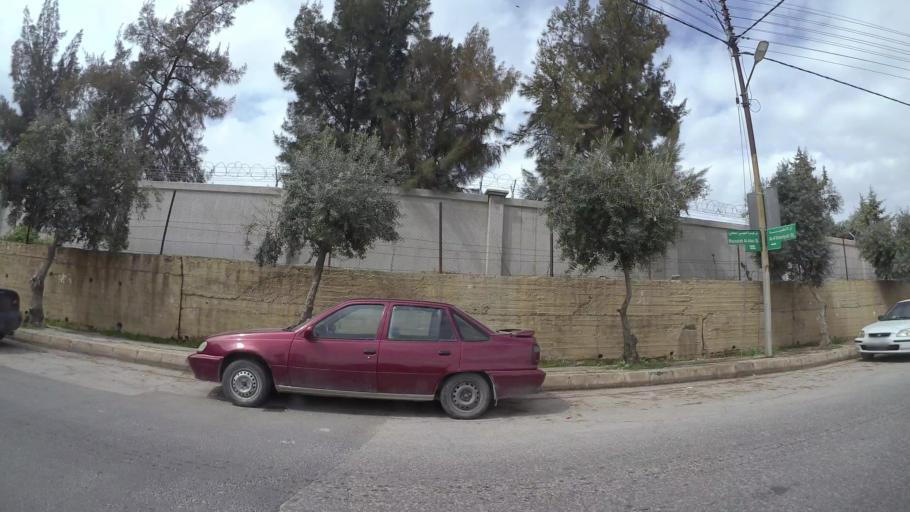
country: JO
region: Amman
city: Amman
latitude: 31.9640
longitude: 35.9493
